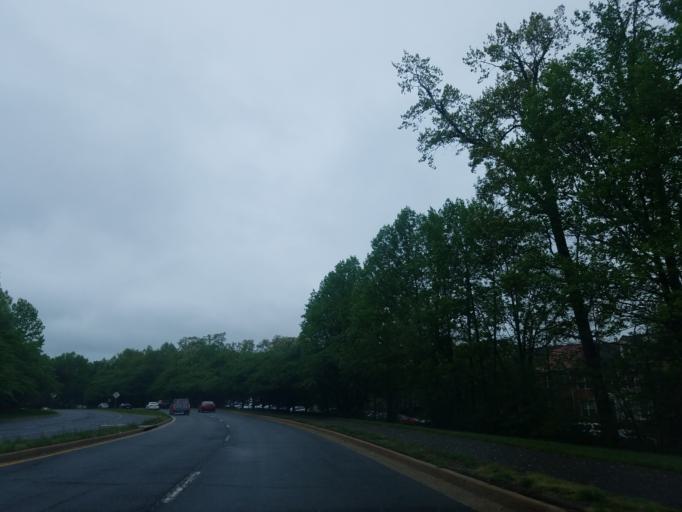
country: US
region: Virginia
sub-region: Fairfax County
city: Dranesville
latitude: 38.9868
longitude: -77.3427
